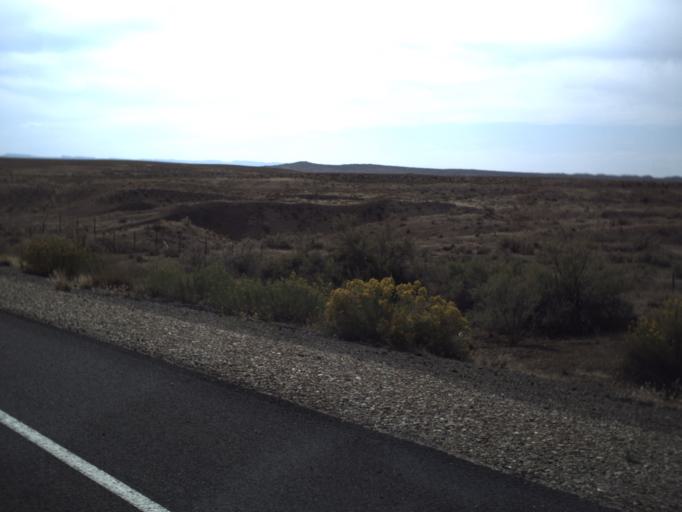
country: US
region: Colorado
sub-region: Mesa County
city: Loma
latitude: 39.0375
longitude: -109.2859
